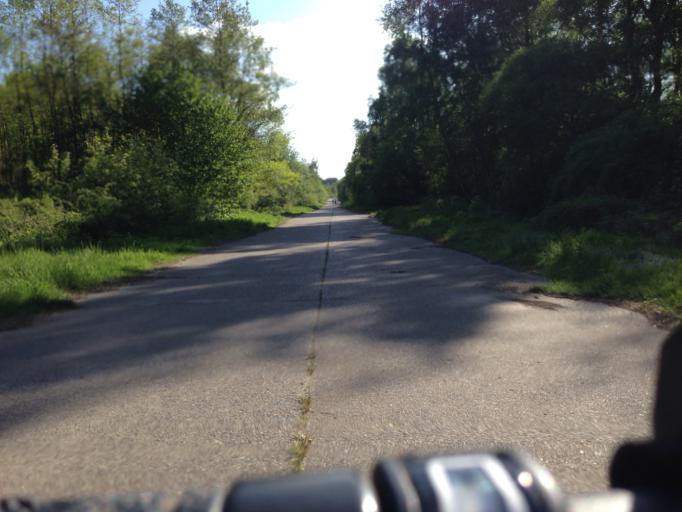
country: DE
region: Schleswig-Holstein
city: Stapelfeld
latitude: 53.6167
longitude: 10.1947
